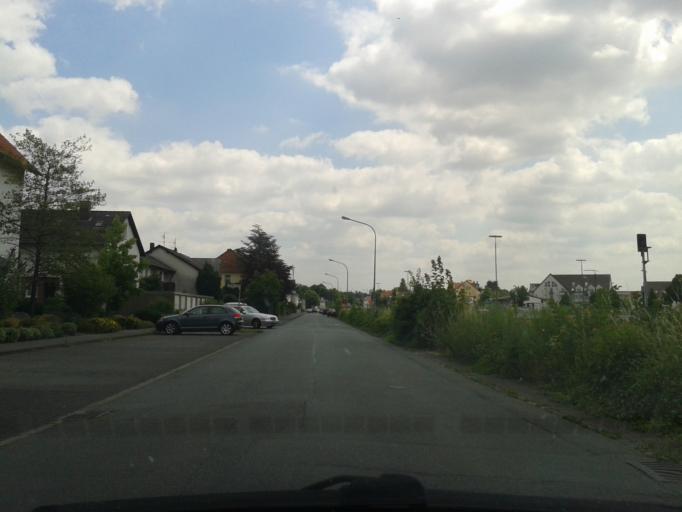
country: DE
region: North Rhine-Westphalia
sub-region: Regierungsbezirk Detmold
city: Paderborn
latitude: 51.7303
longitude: 8.7569
